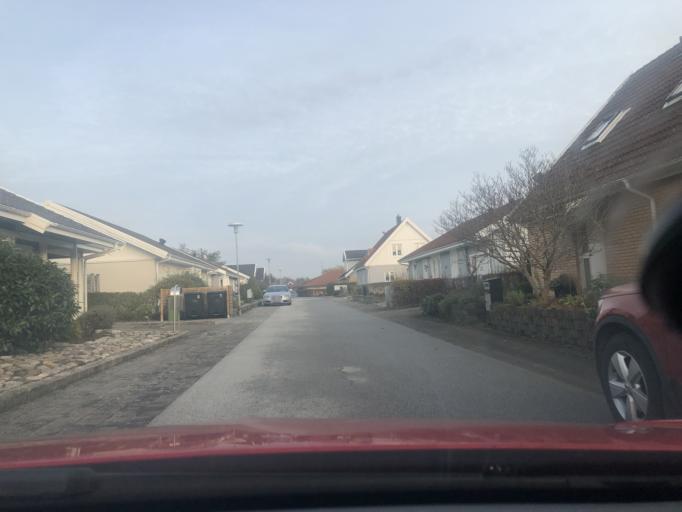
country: SE
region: Skane
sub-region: Burlovs Kommun
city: Arloev
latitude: 55.6050
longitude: 13.0893
